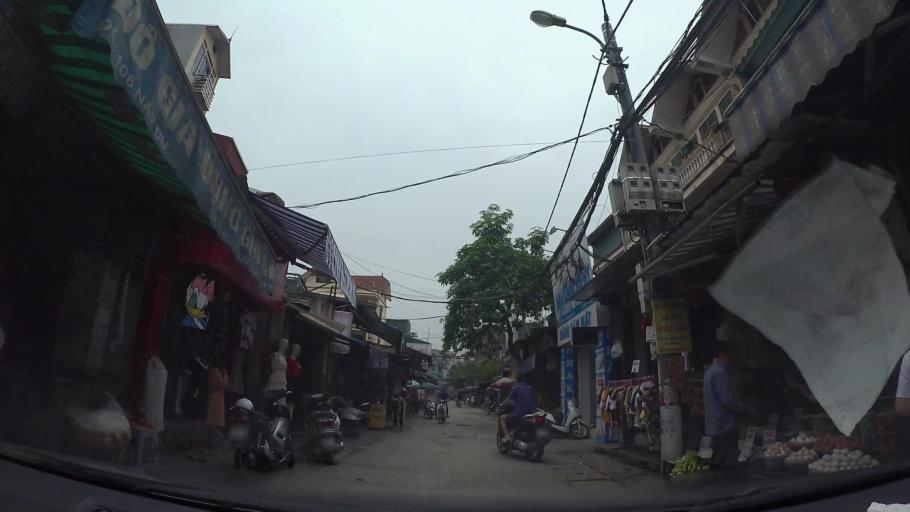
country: VN
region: Ha Noi
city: Hai BaTrung
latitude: 20.9848
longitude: 105.8879
